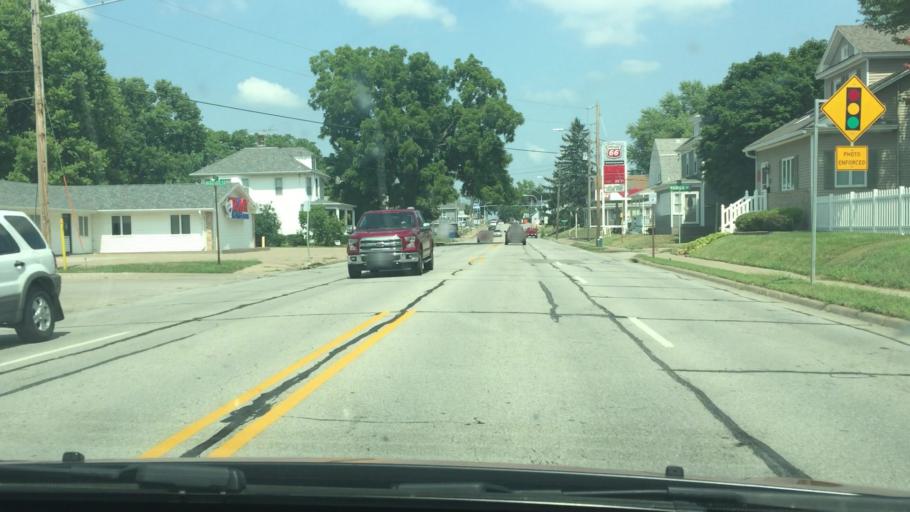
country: US
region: Iowa
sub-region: Muscatine County
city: Muscatine
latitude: 41.4324
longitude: -91.0310
